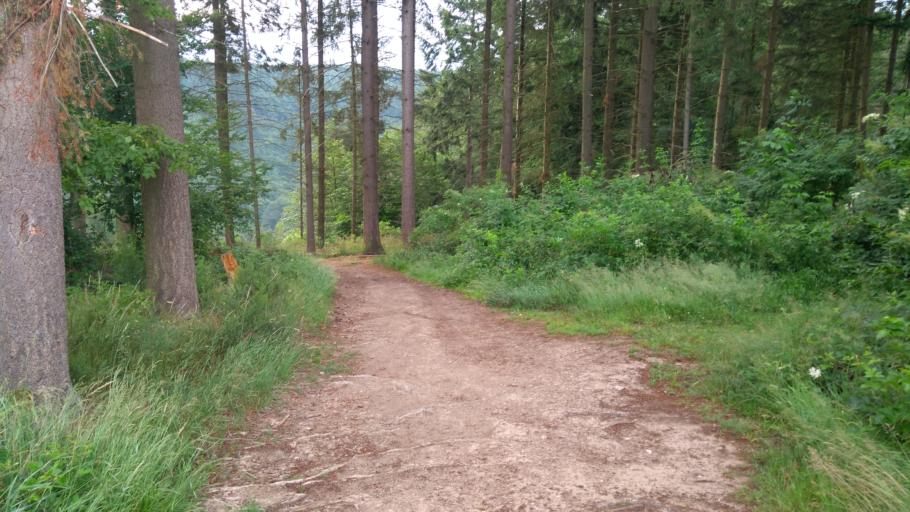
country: DE
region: Rheinland-Pfalz
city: Sosberg
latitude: 50.0886
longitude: 7.3408
